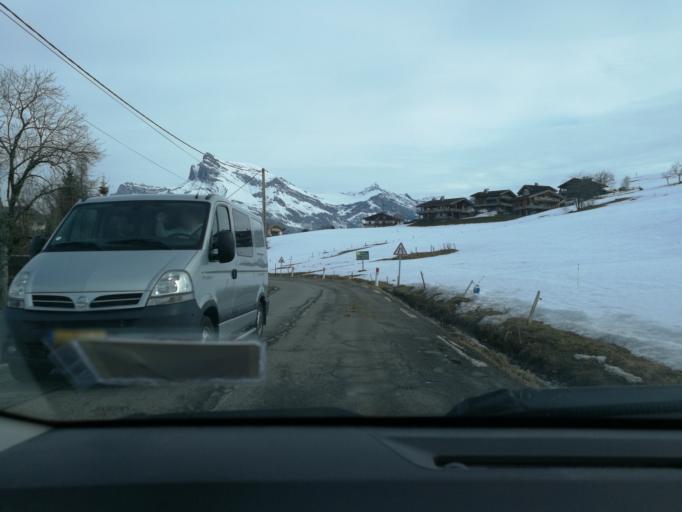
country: FR
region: Rhone-Alpes
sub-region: Departement de la Haute-Savoie
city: Combloux
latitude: 45.8865
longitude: 6.6501
